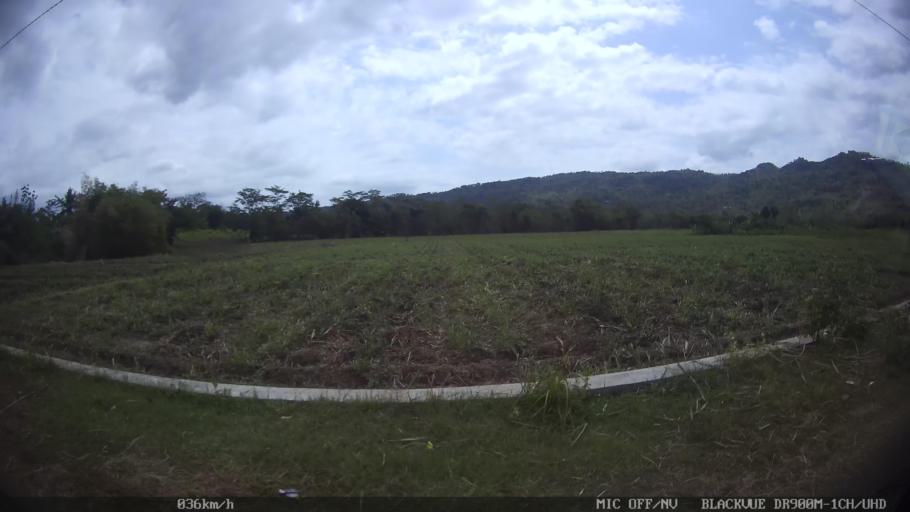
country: ID
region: Central Java
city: Candi Prambanan
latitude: -7.8102
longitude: 110.5059
